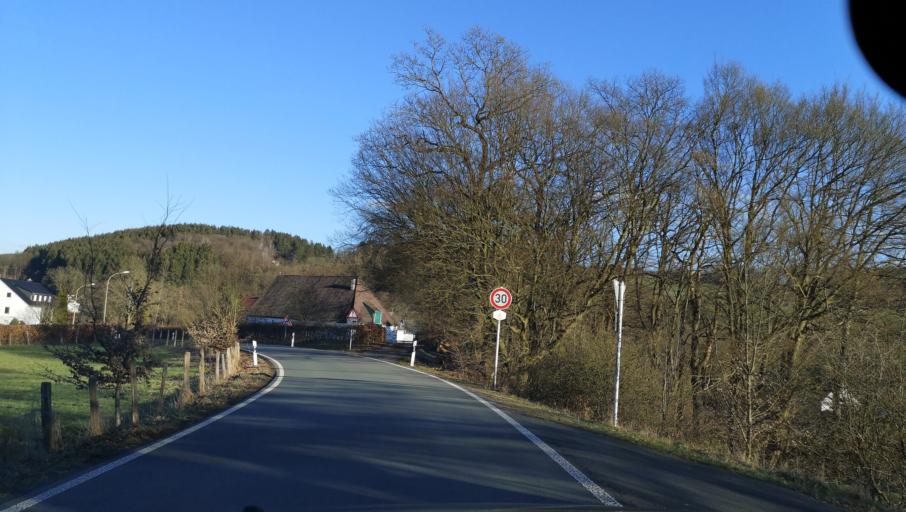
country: DE
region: North Rhine-Westphalia
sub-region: Regierungsbezirk Arnsberg
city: Breckerfeld
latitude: 51.2591
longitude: 7.4212
